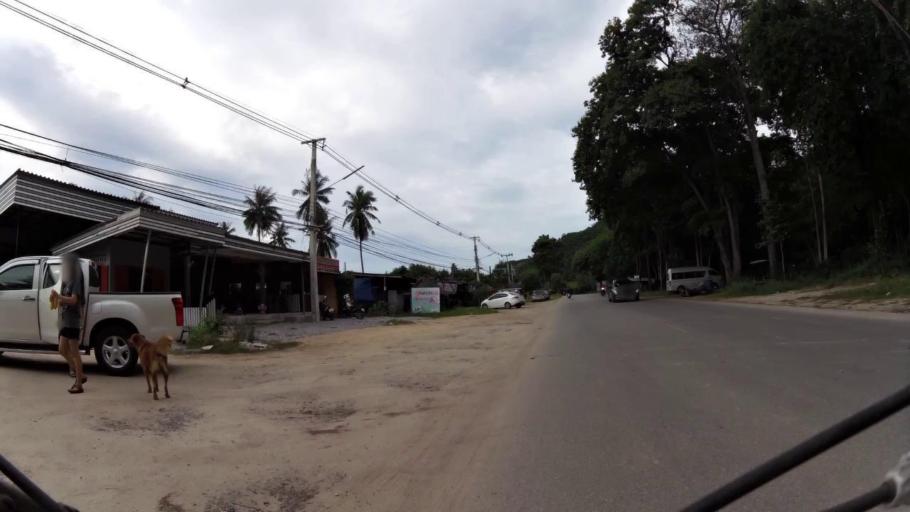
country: TH
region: Prachuap Khiri Khan
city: Prachuap Khiri Khan
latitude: 11.7552
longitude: 99.7920
